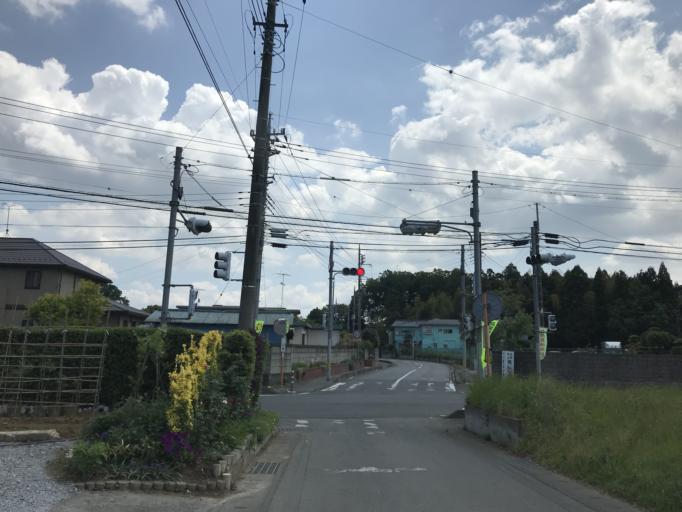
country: JP
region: Ibaraki
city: Mitsukaido
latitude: 36.0685
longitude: 140.0437
